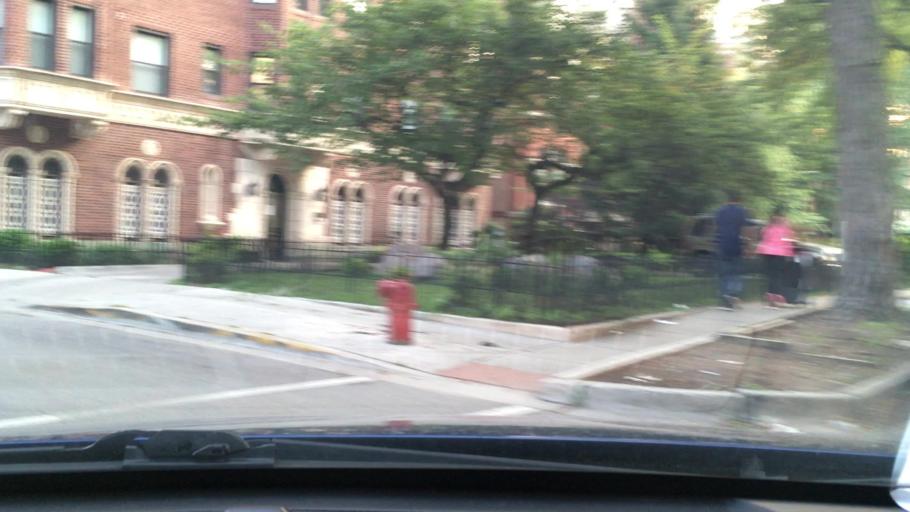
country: US
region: Illinois
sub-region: Cook County
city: Chicago
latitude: 41.9280
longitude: -87.6442
